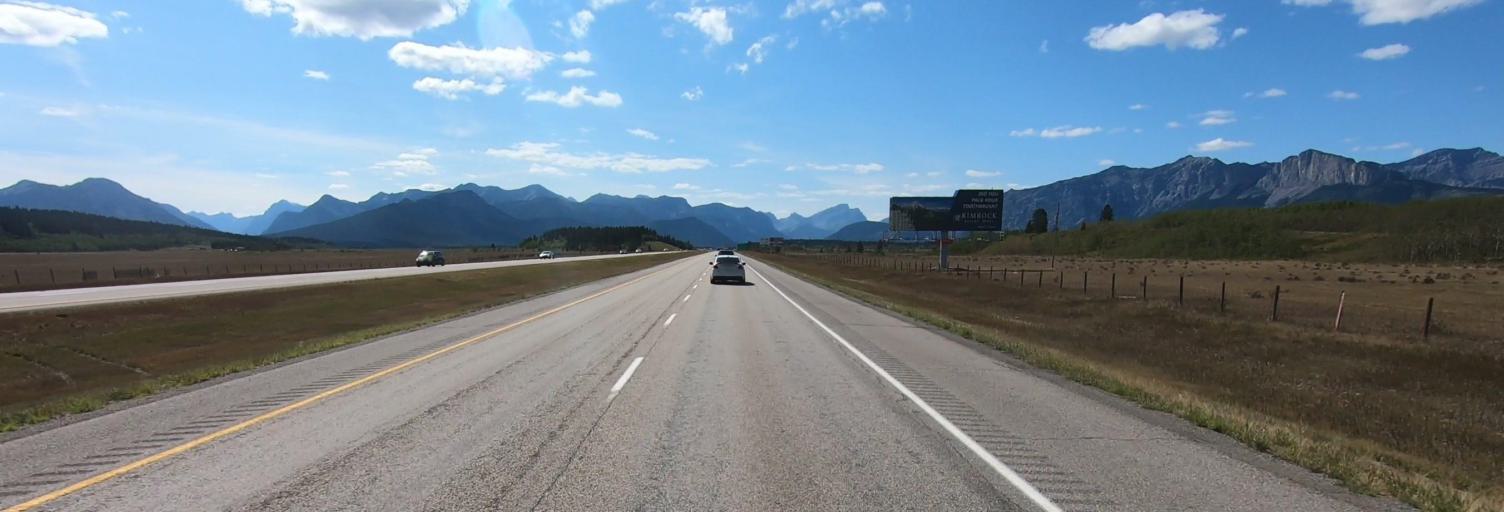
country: CA
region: Alberta
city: Canmore
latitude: 51.1172
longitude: -114.9829
